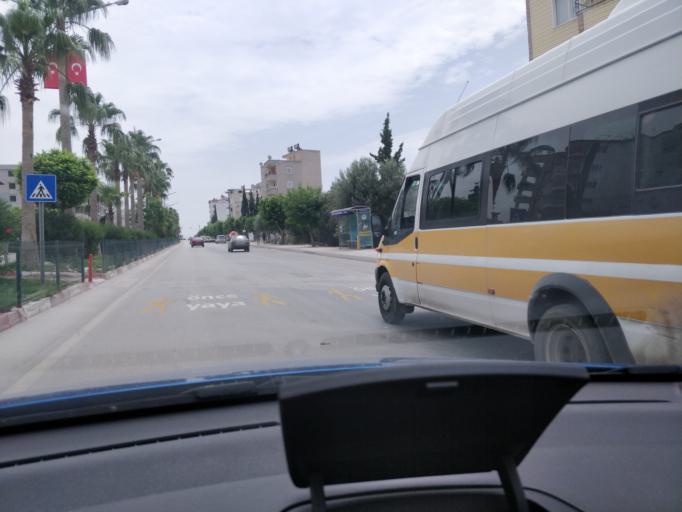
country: TR
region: Mersin
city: Mut
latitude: 36.6402
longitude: 33.4423
